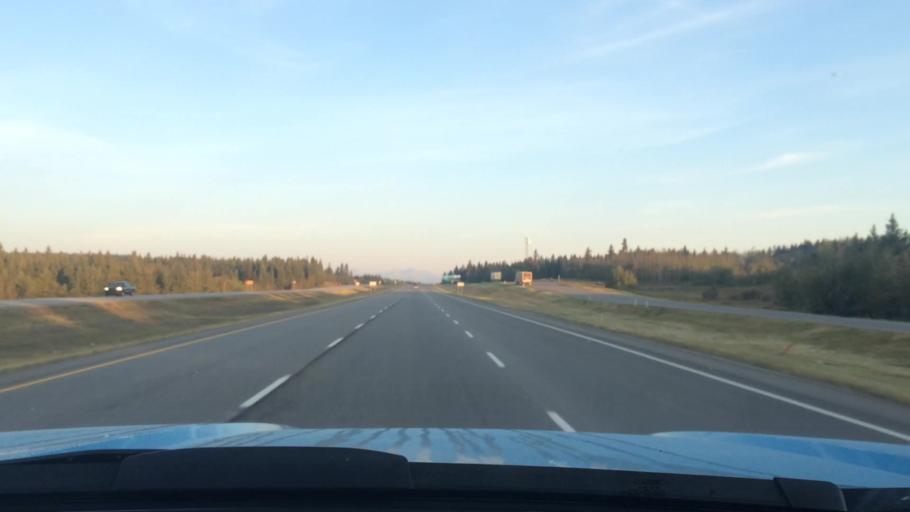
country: CA
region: Alberta
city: Cochrane
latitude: 51.1425
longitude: -114.7221
